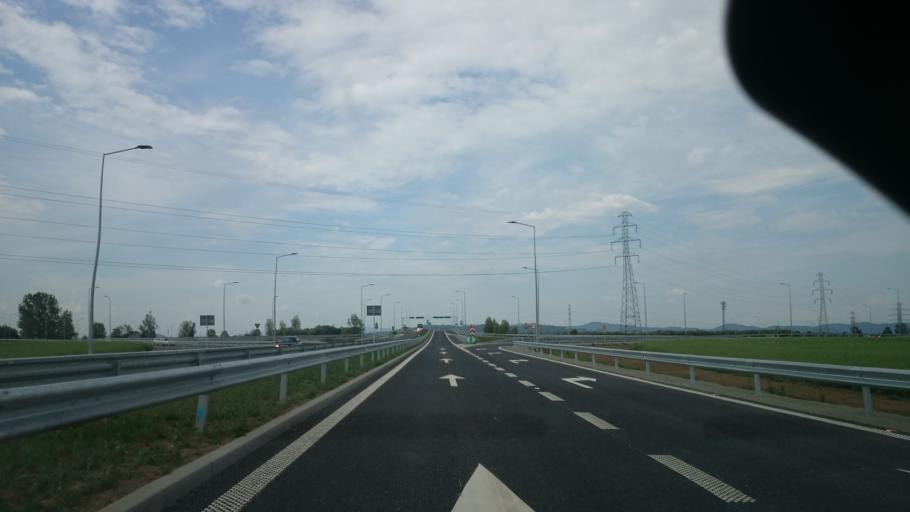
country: PL
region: Lower Silesian Voivodeship
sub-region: Powiat klodzki
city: Klodzko
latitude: 50.4360
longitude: 16.6278
